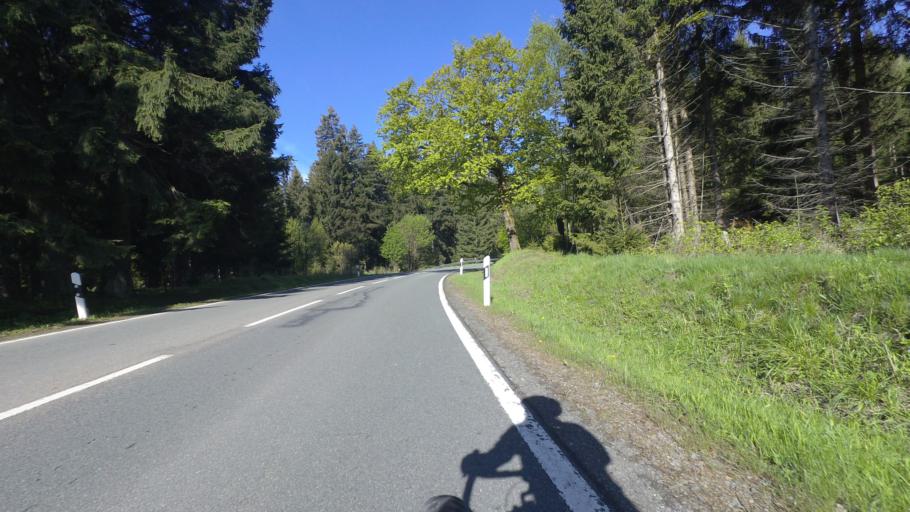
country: DE
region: Saxony-Anhalt
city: Benneckenstein
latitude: 51.7561
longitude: 10.7111
